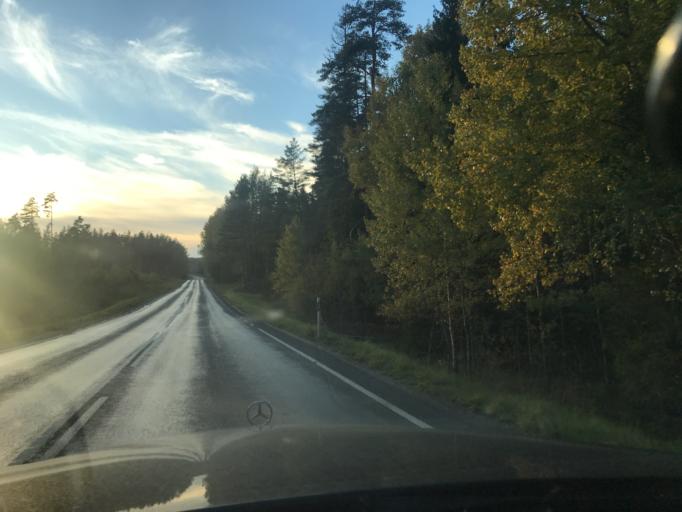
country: EE
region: Vorumaa
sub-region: Antsla vald
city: Vana-Antsla
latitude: 57.8821
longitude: 26.7493
